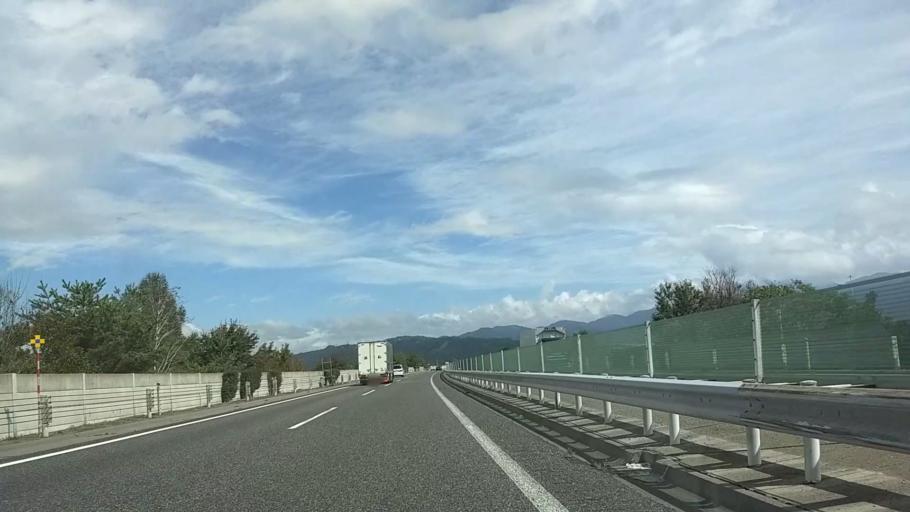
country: JP
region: Nagano
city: Matsumoto
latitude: 36.2178
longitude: 137.9315
